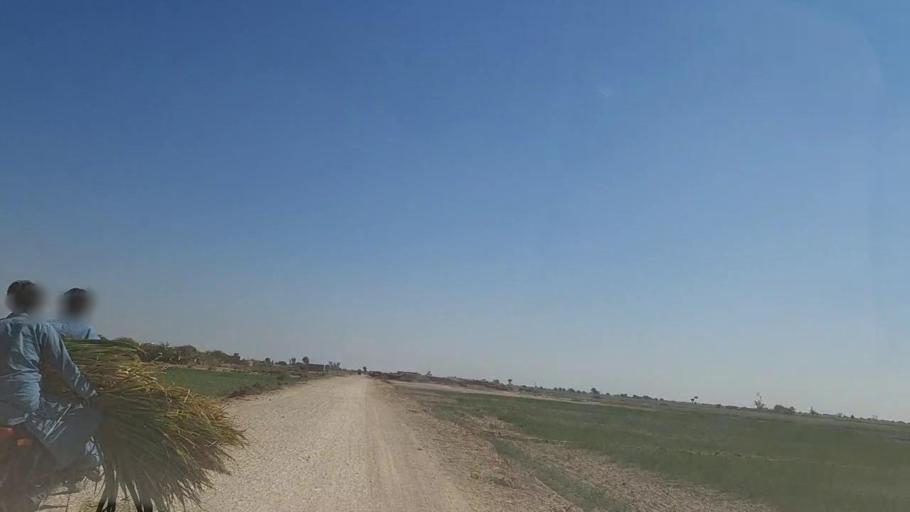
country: PK
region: Sindh
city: Digri
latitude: 25.1173
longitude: 69.1108
